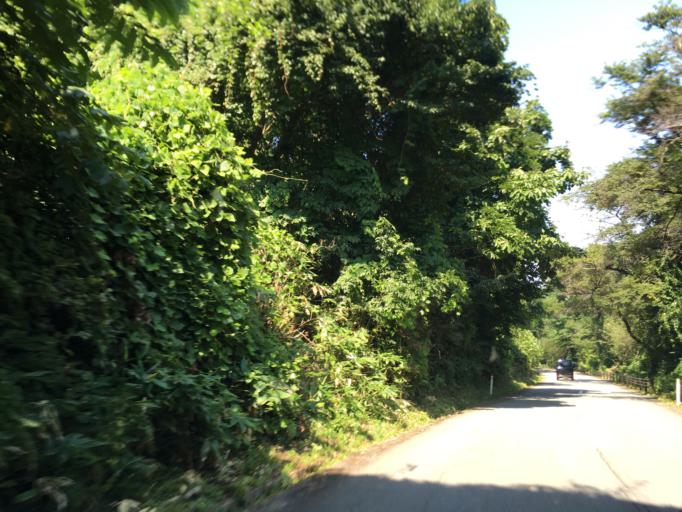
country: JP
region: Akita
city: Tenno
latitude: 39.9296
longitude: 139.8804
